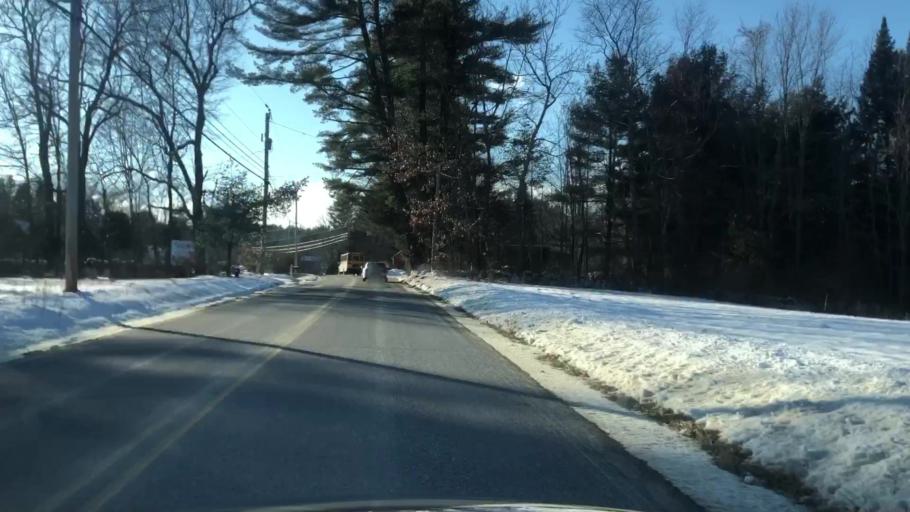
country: US
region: New Hampshire
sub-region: Hillsborough County
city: Milford
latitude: 42.8184
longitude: -71.6852
